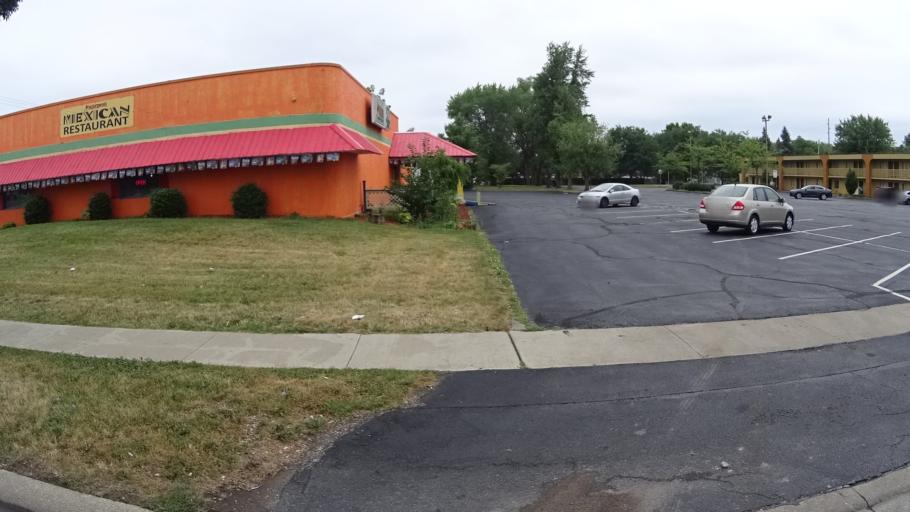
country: US
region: Ohio
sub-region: Erie County
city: Sandusky
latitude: 41.4425
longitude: -82.6855
